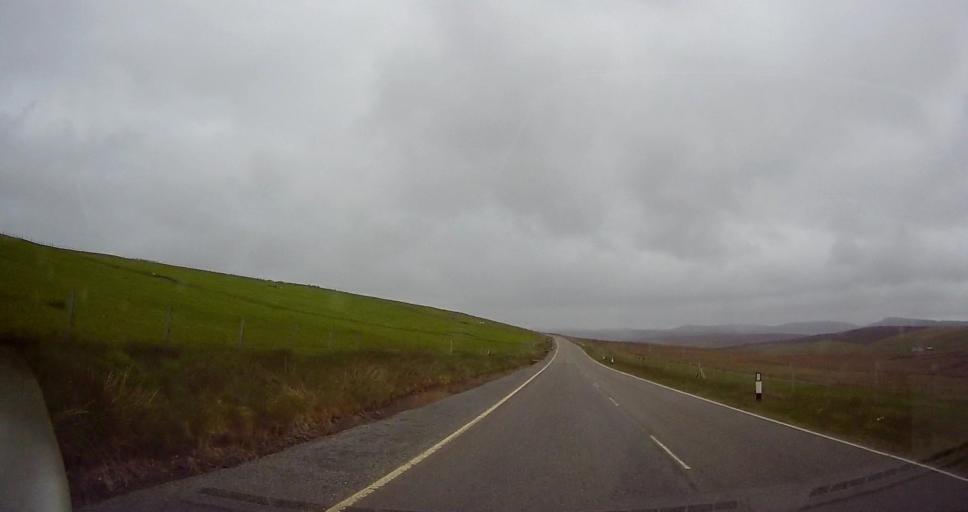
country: GB
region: Scotland
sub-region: Shetland Islands
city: Lerwick
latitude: 60.2653
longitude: -1.3972
